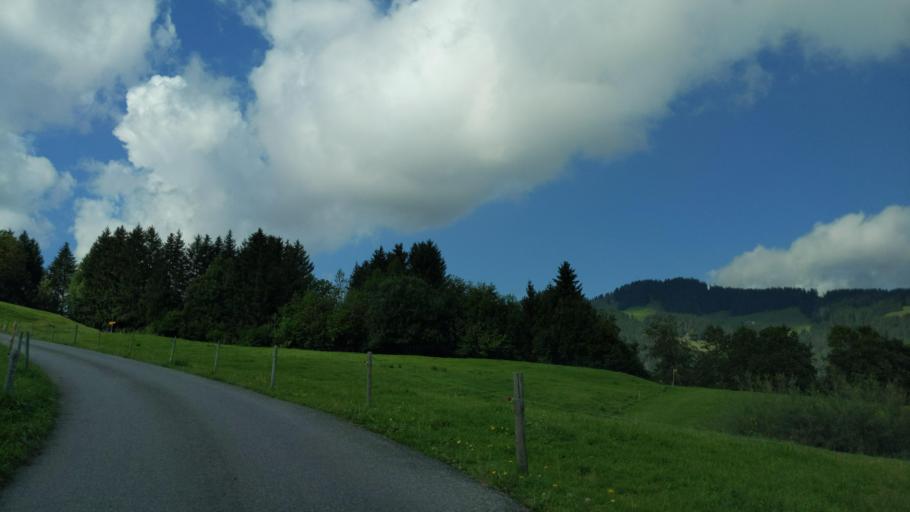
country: CH
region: Appenzell Innerrhoden
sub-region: Appenzell Inner Rhodes
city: Appenzell
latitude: 47.2997
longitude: 9.4261
